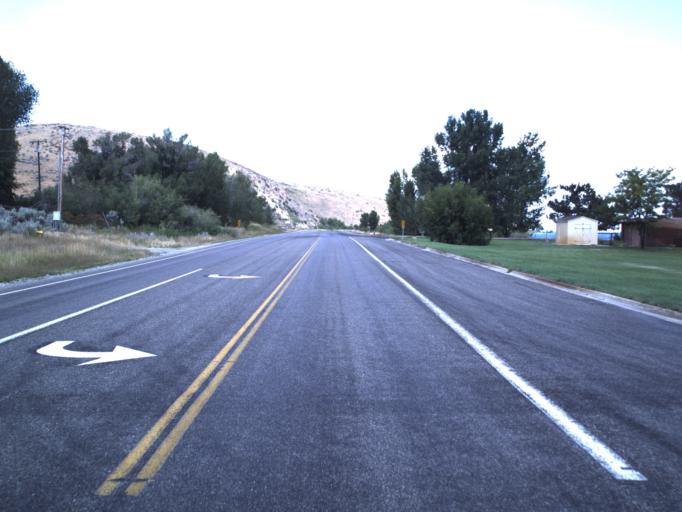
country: US
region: Utah
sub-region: Rich County
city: Randolph
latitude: 41.8561
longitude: -111.3641
